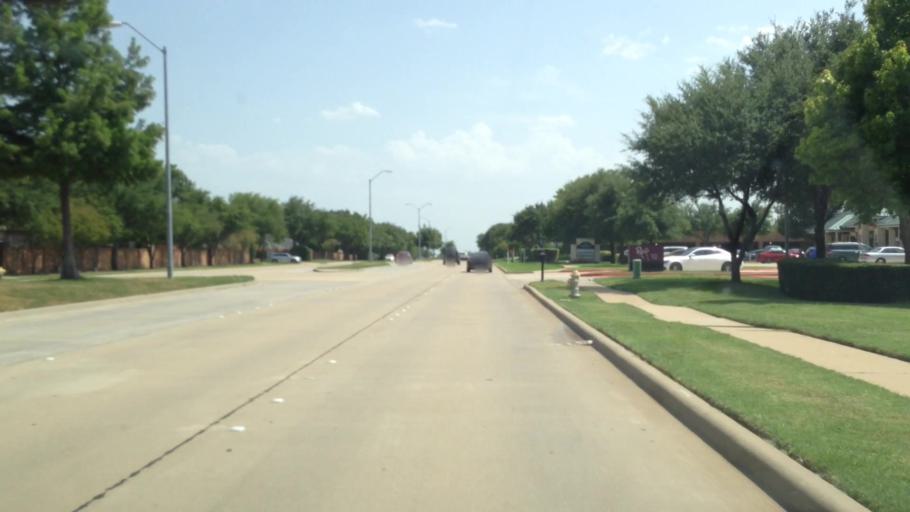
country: US
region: Texas
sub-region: Denton County
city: The Colony
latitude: 33.0409
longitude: -96.8275
